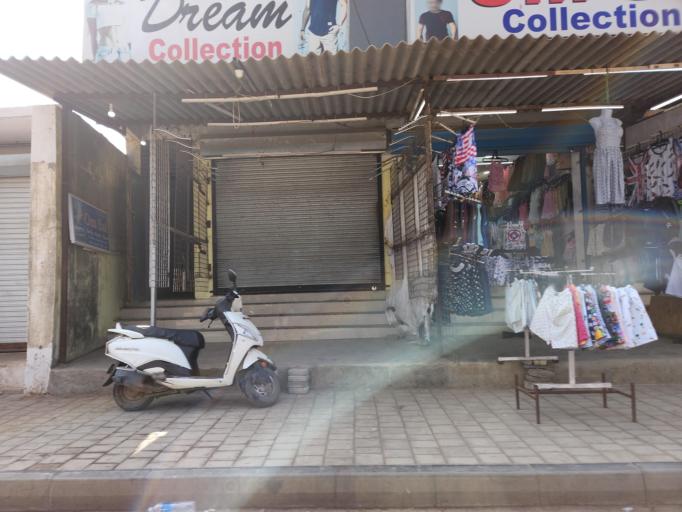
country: IN
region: Daman and Diu
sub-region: Daman District
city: Daman
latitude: 20.3777
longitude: 72.8245
